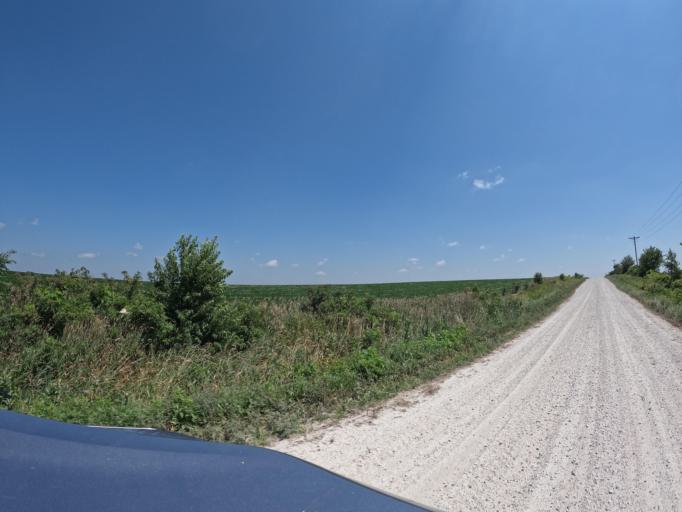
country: US
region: Iowa
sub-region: Keokuk County
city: Sigourney
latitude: 41.2794
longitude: -92.2337
